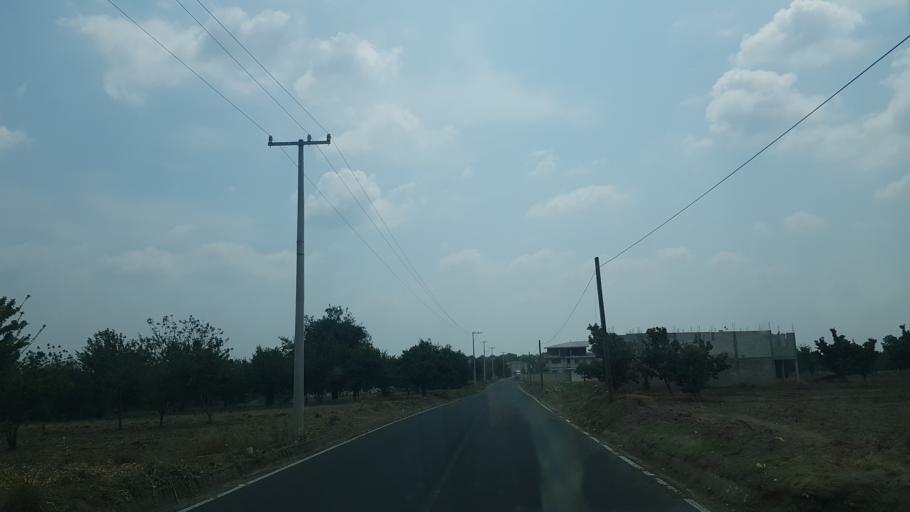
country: MX
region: Puebla
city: Domingo Arenas
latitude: 19.1418
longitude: -98.4742
